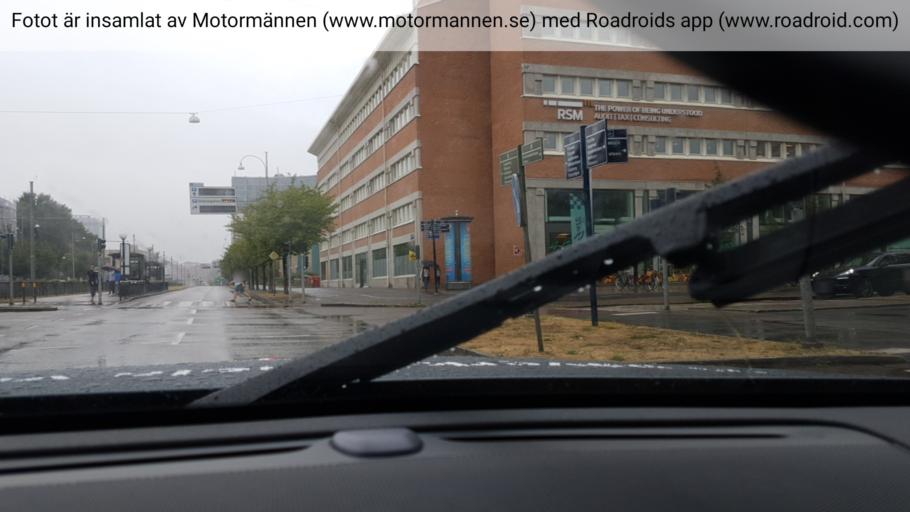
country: SE
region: Vaestra Goetaland
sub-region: Goteborg
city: Goeteborg
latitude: 57.7060
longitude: 11.9841
